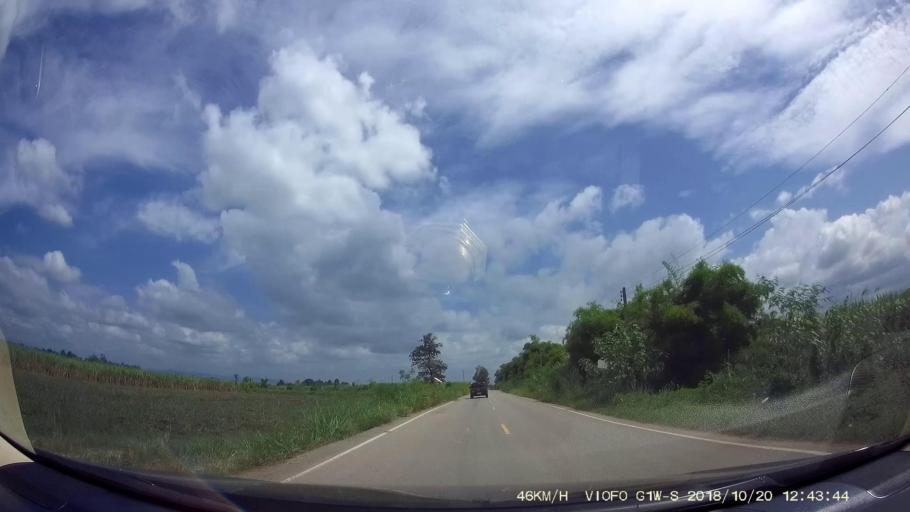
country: TH
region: Chaiyaphum
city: Khon San
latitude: 16.5411
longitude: 101.8633
